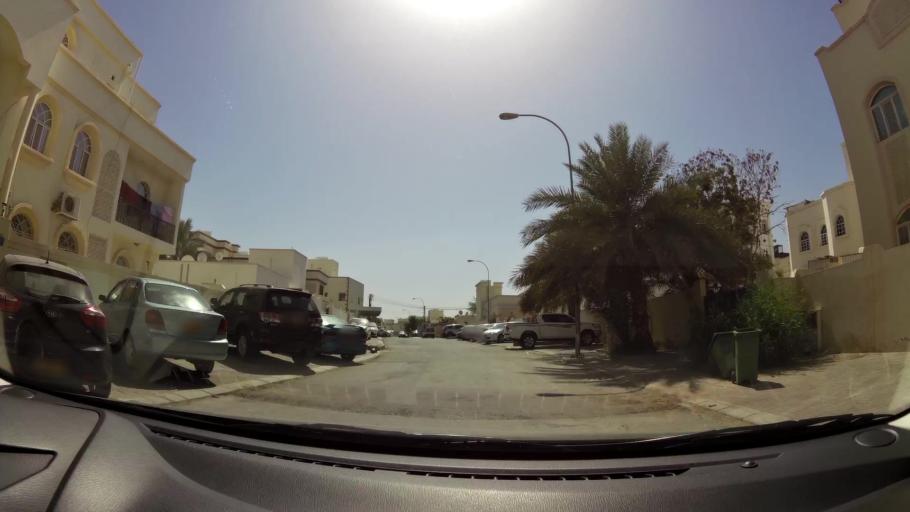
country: OM
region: Muhafazat Masqat
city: Bawshar
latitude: 23.6018
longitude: 58.3816
